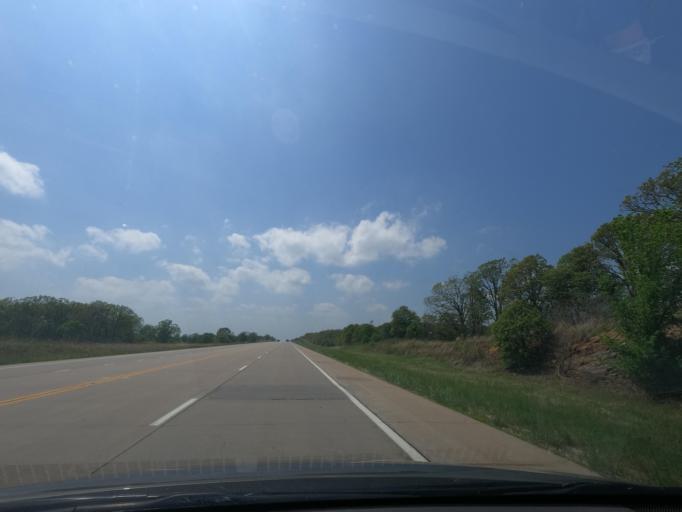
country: US
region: Kansas
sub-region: Wilson County
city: Fredonia
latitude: 37.6142
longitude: -95.9085
